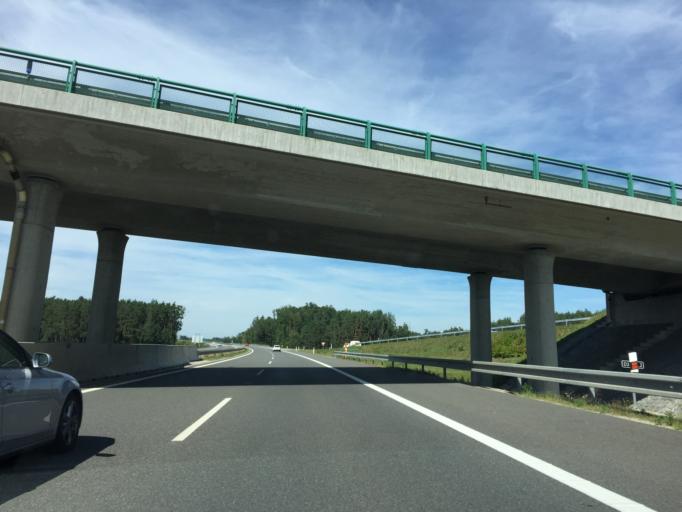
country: CZ
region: Jihocesky
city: Sobeslav
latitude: 49.2231
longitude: 14.7278
